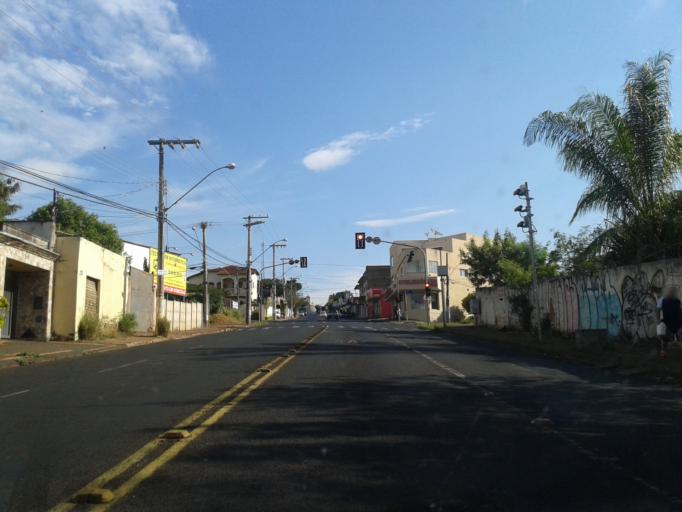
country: BR
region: Minas Gerais
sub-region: Uberlandia
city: Uberlandia
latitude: -18.9324
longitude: -48.2957
